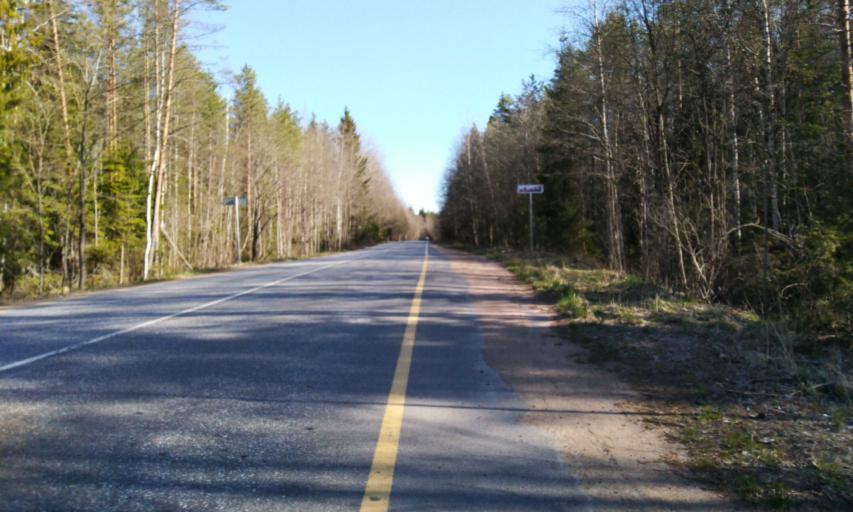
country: RU
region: Leningrad
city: Garbolovo
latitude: 60.3413
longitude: 30.4361
